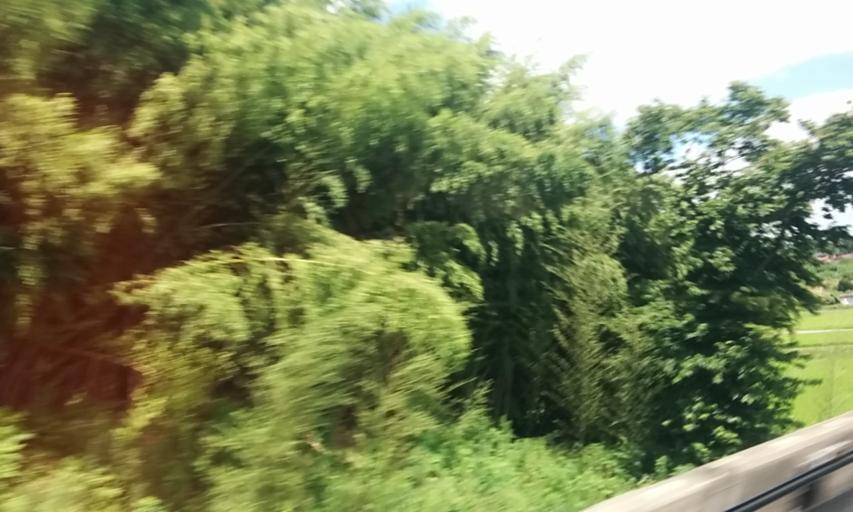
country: JP
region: Fukushima
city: Motomiya
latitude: 37.5151
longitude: 140.4315
